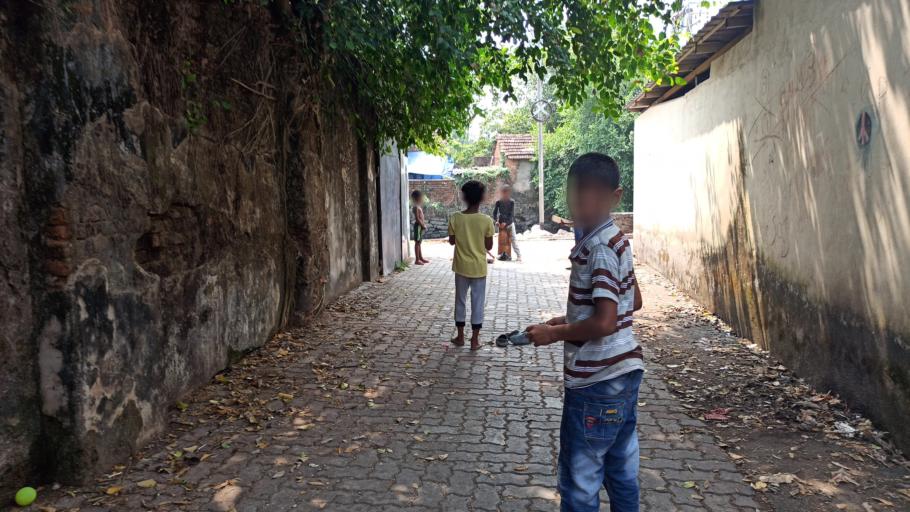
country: IN
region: Kerala
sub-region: Ernakulam
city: Cochin
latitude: 9.9680
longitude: 76.2500
